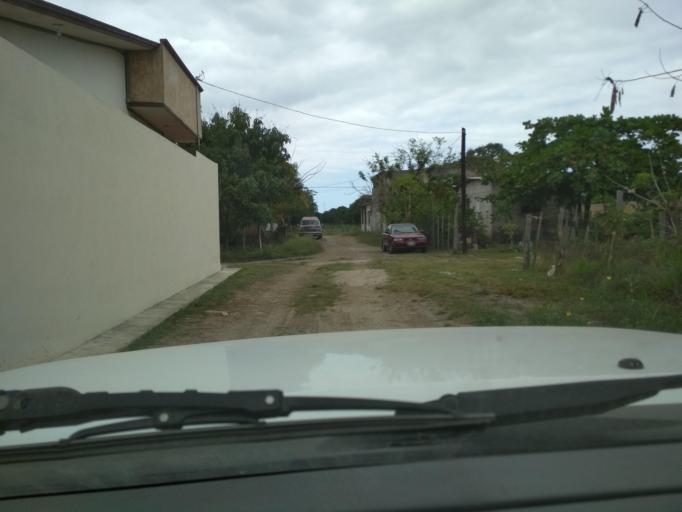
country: MX
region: Veracruz
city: El Tejar
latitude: 19.0731
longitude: -96.1478
